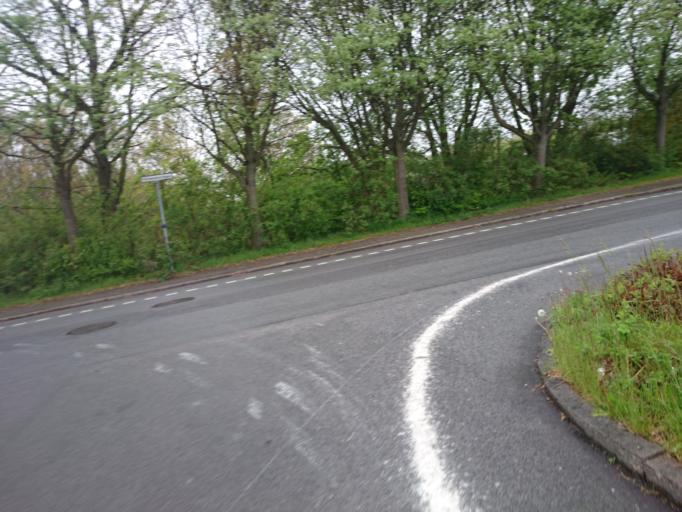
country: SE
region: Skane
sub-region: Lunds Kommun
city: Lund
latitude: 55.7063
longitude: 13.2350
